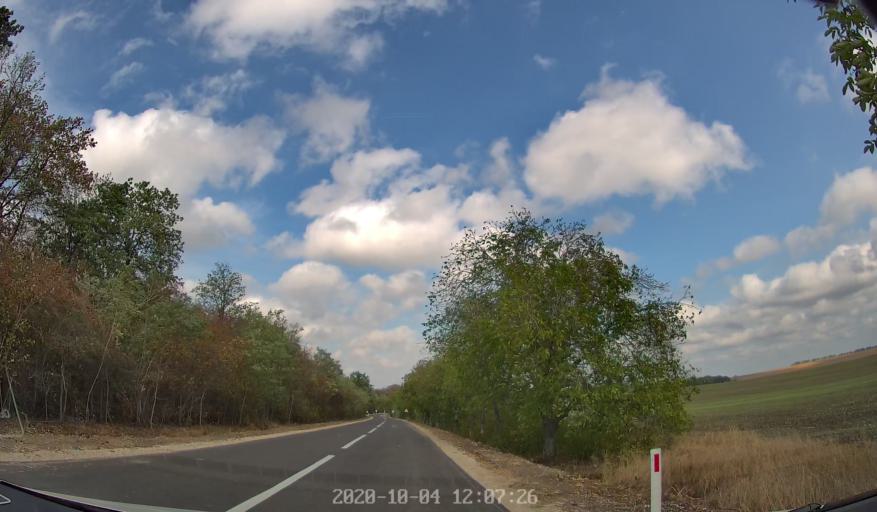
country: MD
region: Rezina
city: Saharna
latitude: 47.5860
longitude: 28.9716
